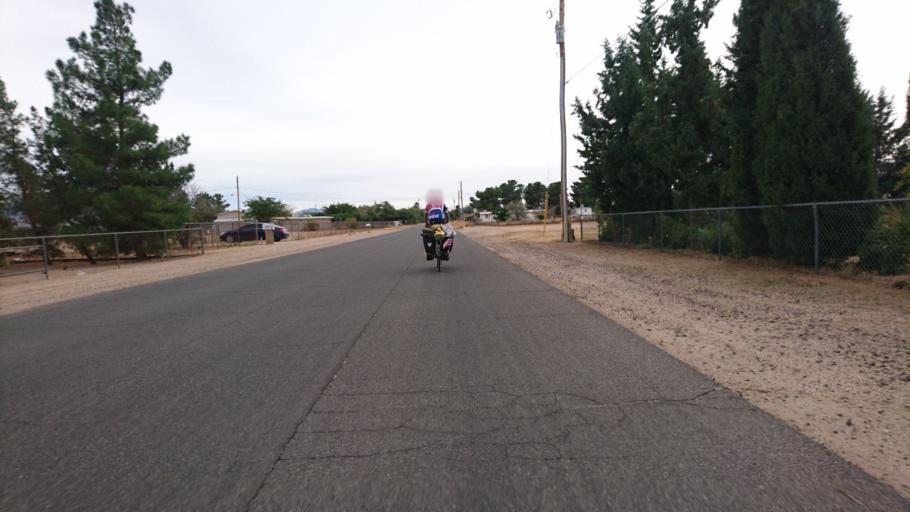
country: US
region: Arizona
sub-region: Mohave County
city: New Kingman-Butler
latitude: 35.2373
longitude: -114.0183
